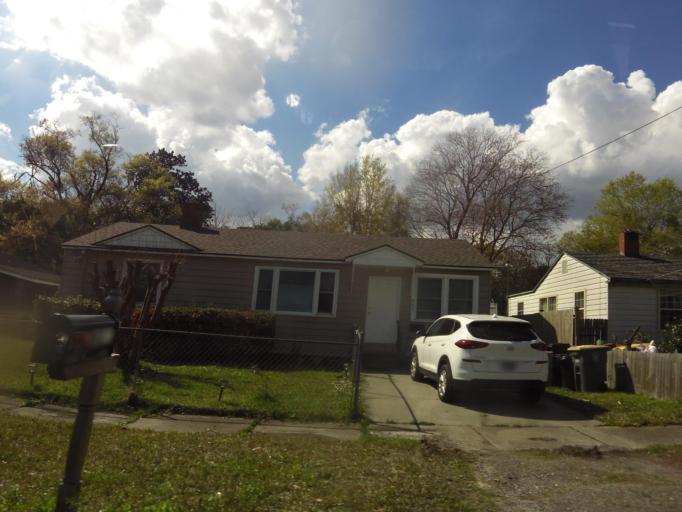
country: US
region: Florida
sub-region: Duval County
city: Jacksonville
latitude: 30.3363
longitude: -81.7141
